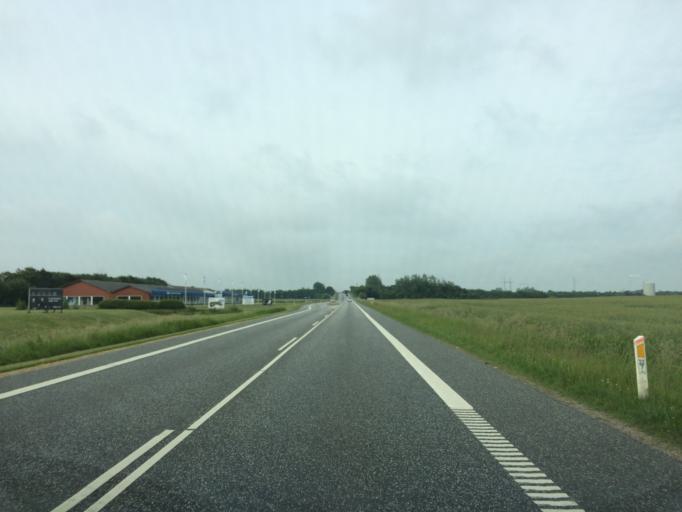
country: DK
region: Central Jutland
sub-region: Holstebro Kommune
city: Ulfborg
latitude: 56.2847
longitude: 8.3322
